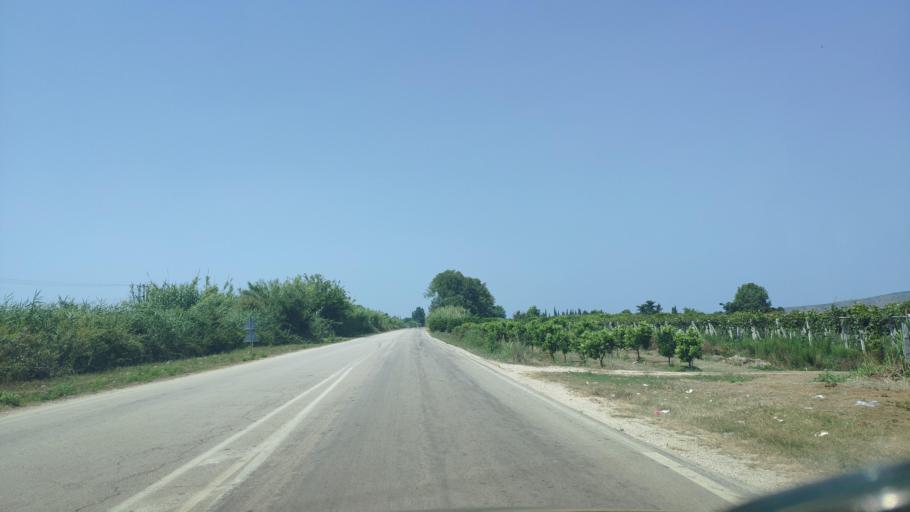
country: GR
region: Epirus
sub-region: Nomos Artas
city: Aneza
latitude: 39.1176
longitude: 20.9315
